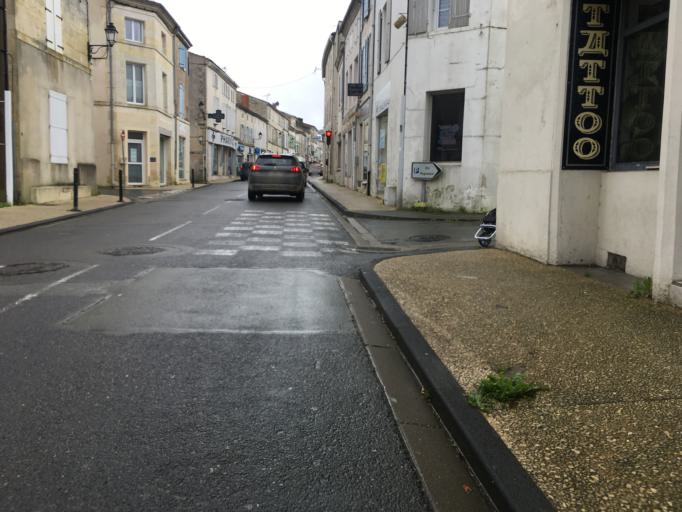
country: FR
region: Poitou-Charentes
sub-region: Departement de la Charente-Maritime
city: Surgeres
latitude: 46.1082
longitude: -0.7530
